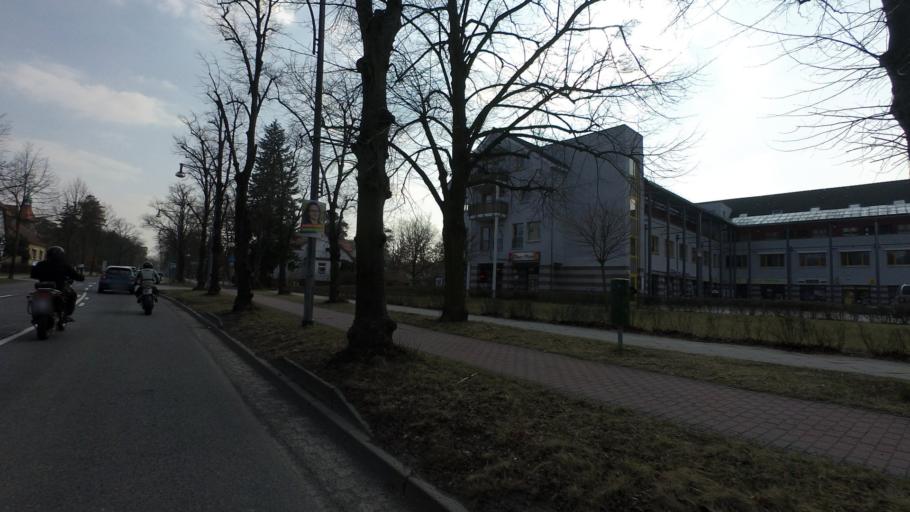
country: DE
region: Brandenburg
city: Potsdam
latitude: 52.3495
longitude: 13.1043
